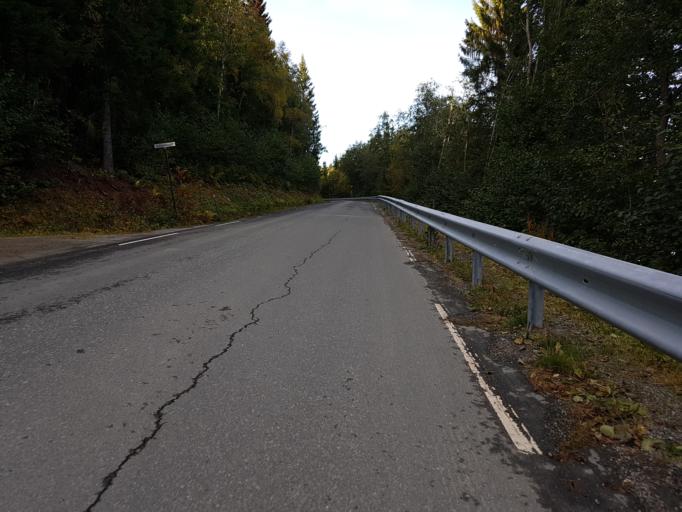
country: NO
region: Sor-Trondelag
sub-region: Klaebu
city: Klaebu
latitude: 63.3423
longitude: 10.5544
